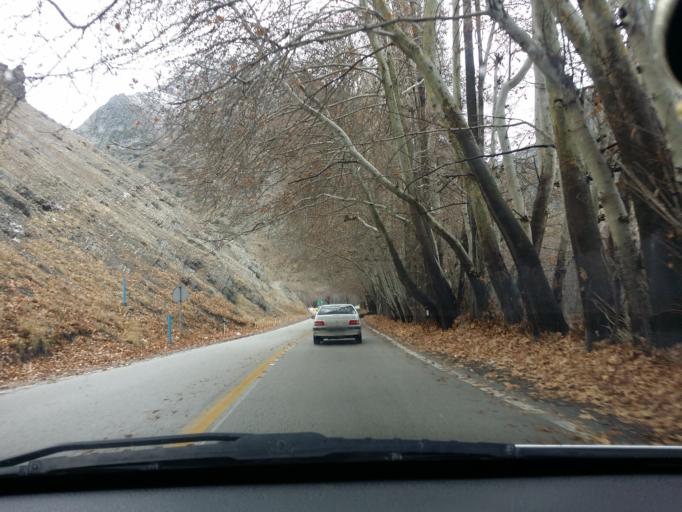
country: IR
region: Tehran
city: Tajrish
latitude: 36.0262
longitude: 51.2469
